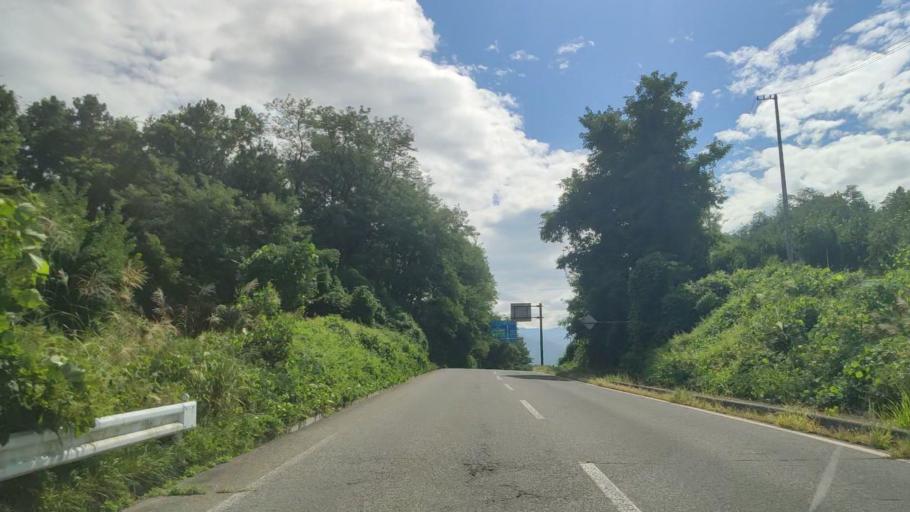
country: JP
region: Nagano
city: Nakano
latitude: 36.7355
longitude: 138.3057
